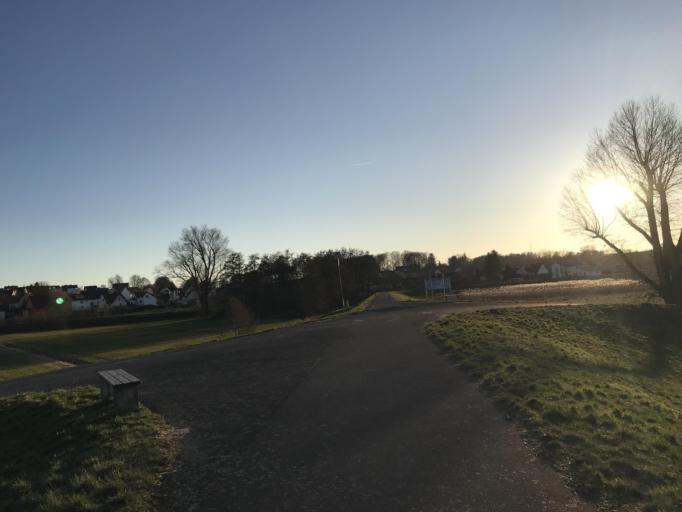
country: DE
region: Hesse
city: Schwalmstadt
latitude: 50.9075
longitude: 9.2208
